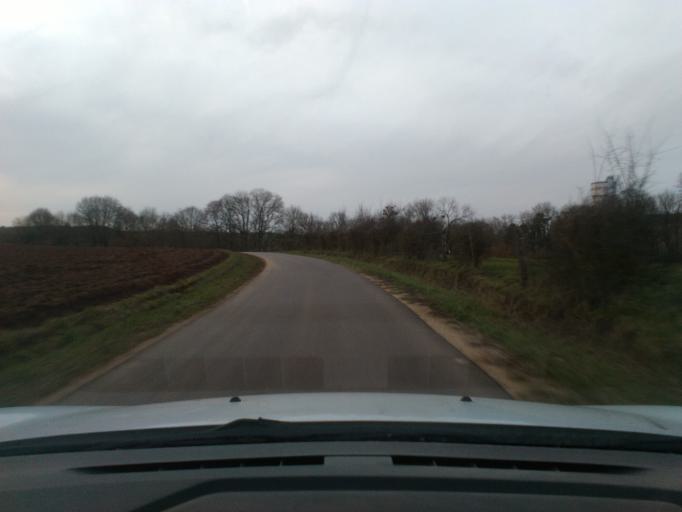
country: FR
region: Lorraine
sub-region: Departement des Vosges
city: Mirecourt
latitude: 48.2873
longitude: 6.1121
